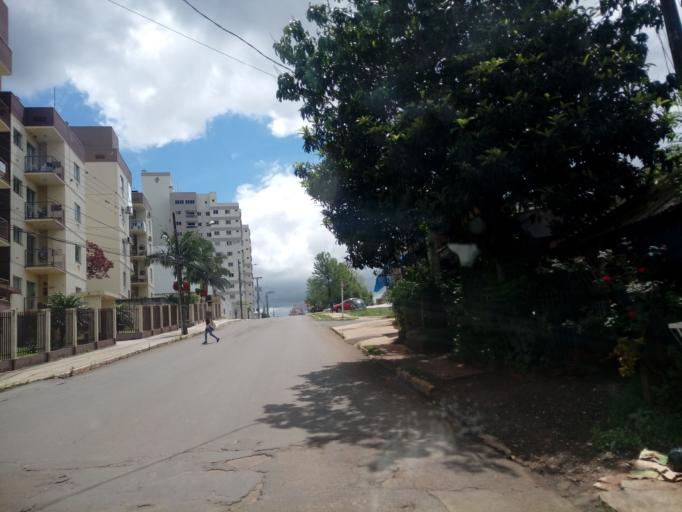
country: BR
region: Santa Catarina
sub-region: Chapeco
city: Chapeco
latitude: -27.0982
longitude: -52.6381
